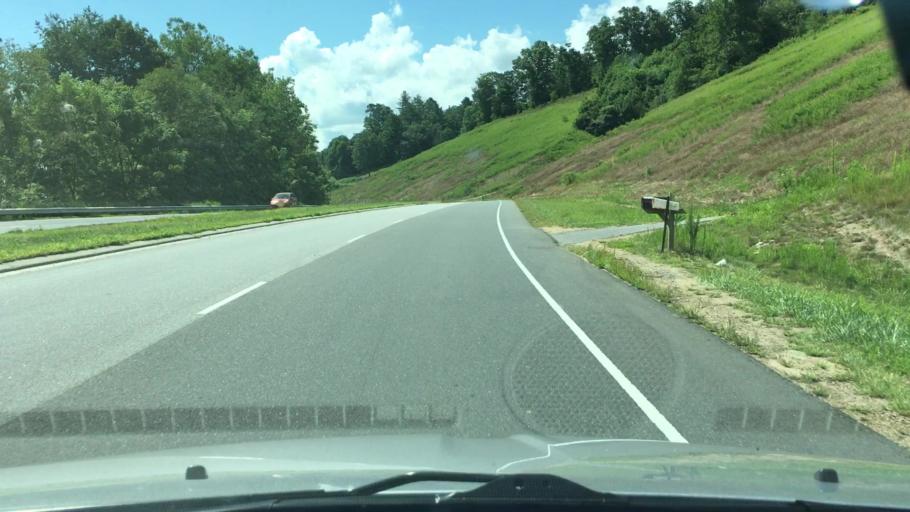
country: US
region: North Carolina
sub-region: Yancey County
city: Burnsville
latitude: 35.9154
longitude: -82.2442
